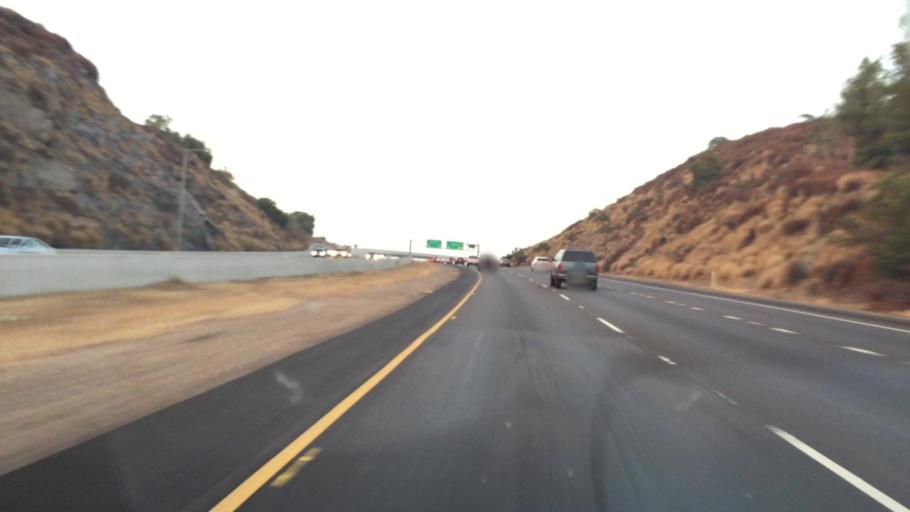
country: US
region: California
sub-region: San Diego County
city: Santee
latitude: 32.8393
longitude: -116.9621
